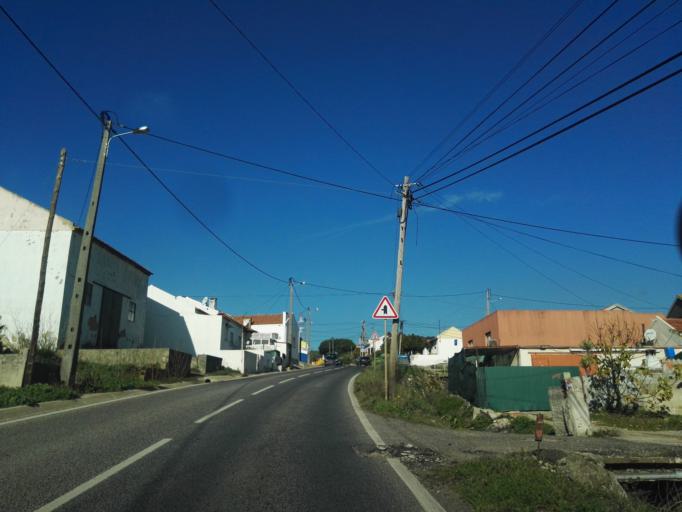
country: PT
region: Lisbon
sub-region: Loures
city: Loures
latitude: 38.8662
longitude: -9.1827
